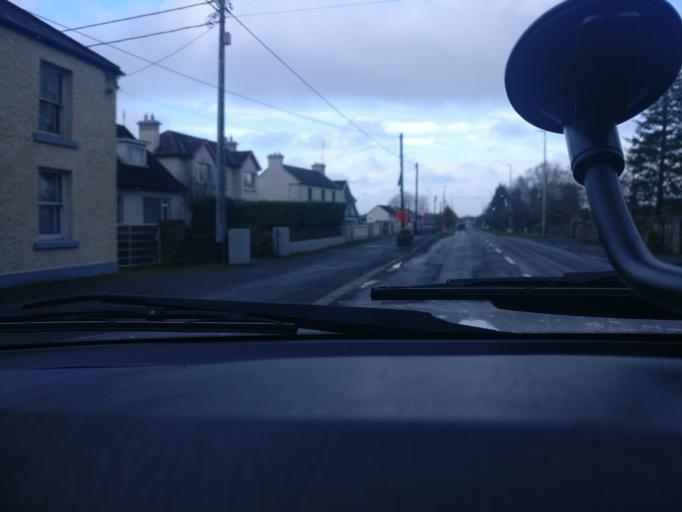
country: IE
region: Connaught
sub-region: County Galway
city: Athenry
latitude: 53.2314
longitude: -8.7368
